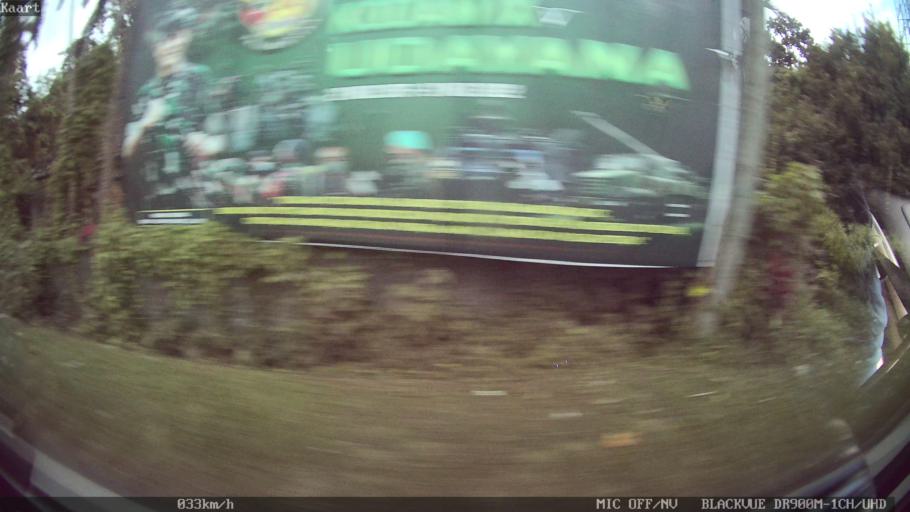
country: ID
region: Bali
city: Pohgending Kangin
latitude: -8.4263
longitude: 115.1445
